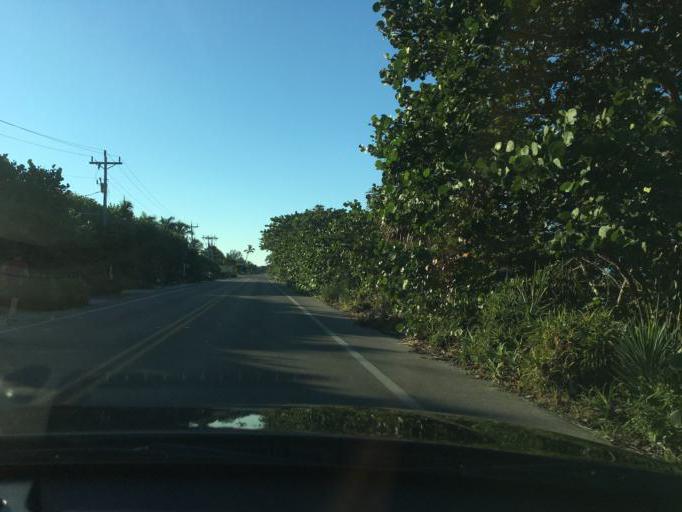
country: US
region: Florida
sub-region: Lee County
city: Saint James City
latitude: 26.5124
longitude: -82.1910
